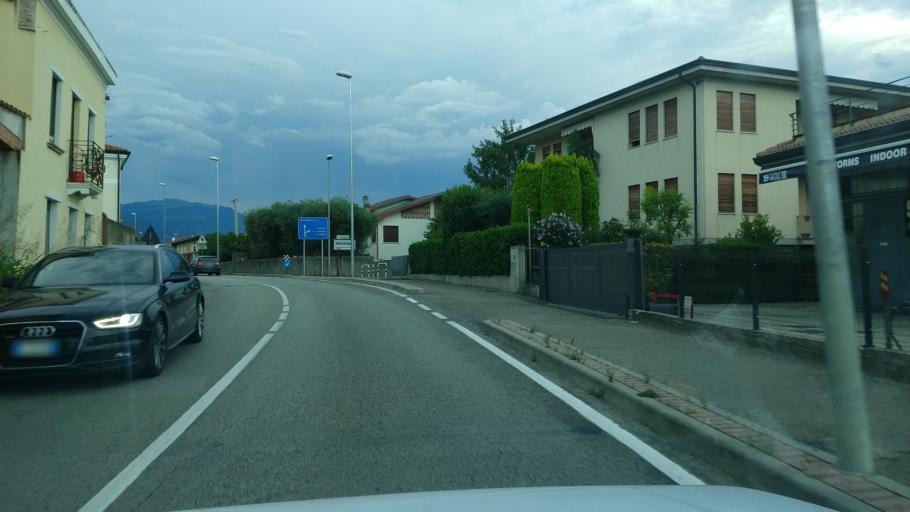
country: IT
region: Veneto
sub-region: Provincia di Vicenza
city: Nove
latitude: 45.7355
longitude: 11.6884
